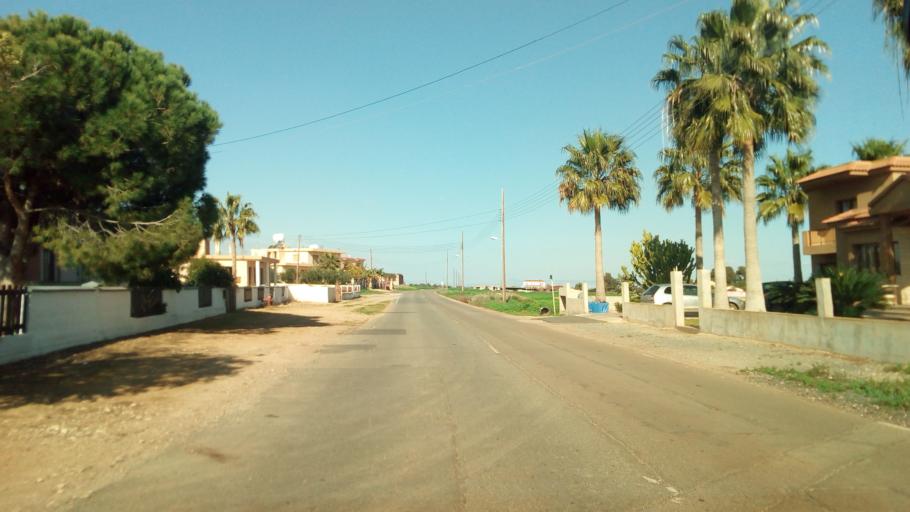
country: CY
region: Ammochostos
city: Avgorou
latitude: 34.9890
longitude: 33.8478
